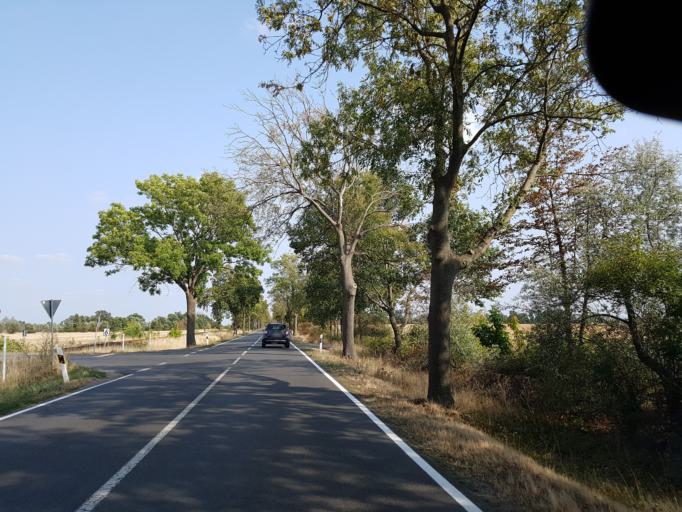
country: DE
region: Saxony-Anhalt
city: Kemberg
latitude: 51.7971
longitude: 12.6969
